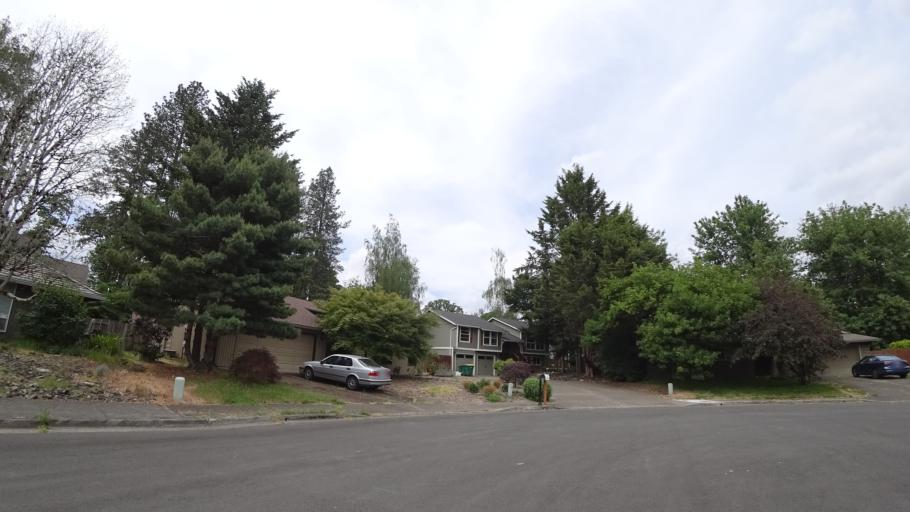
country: US
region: Oregon
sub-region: Washington County
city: Metzger
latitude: 45.4545
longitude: -122.7681
